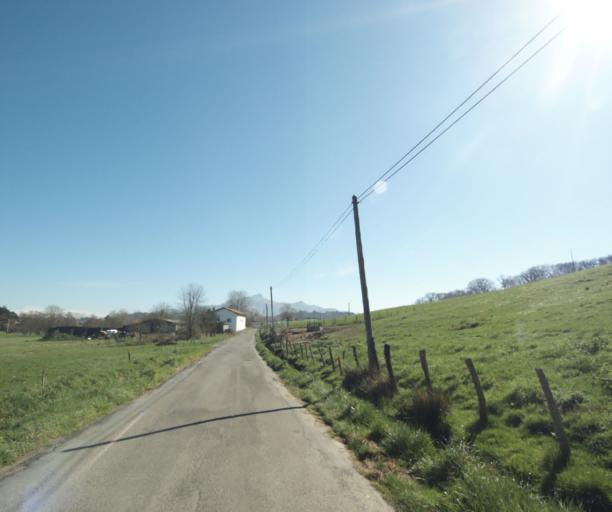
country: FR
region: Aquitaine
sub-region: Departement des Pyrenees-Atlantiques
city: Ciboure
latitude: 43.3767
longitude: -1.6898
